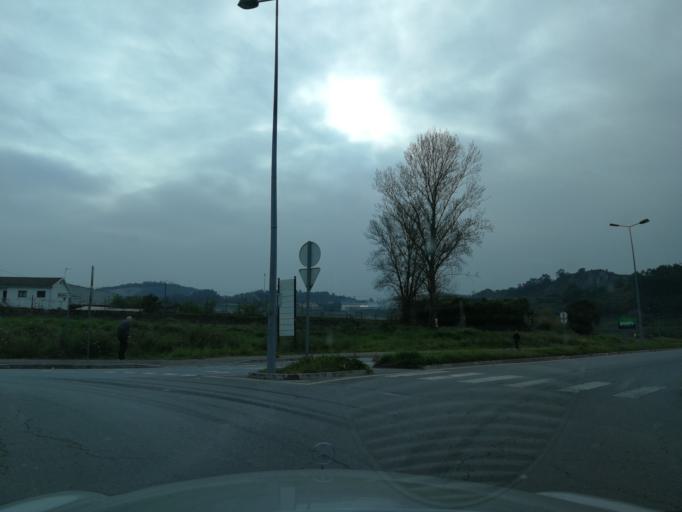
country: PT
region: Braga
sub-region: Braga
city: Braga
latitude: 41.5654
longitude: -8.4396
